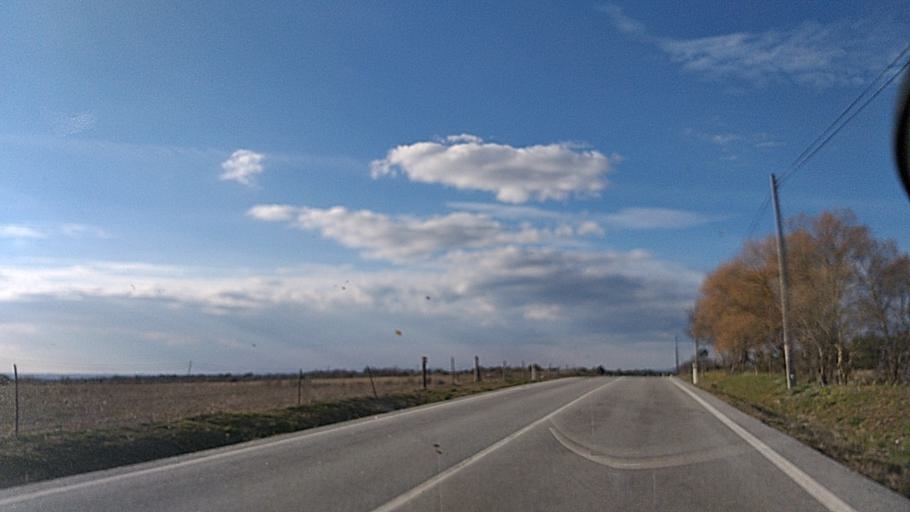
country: ES
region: Castille and Leon
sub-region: Provincia de Salamanca
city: Fuentes de Onoro
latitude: 40.6248
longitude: -6.8480
